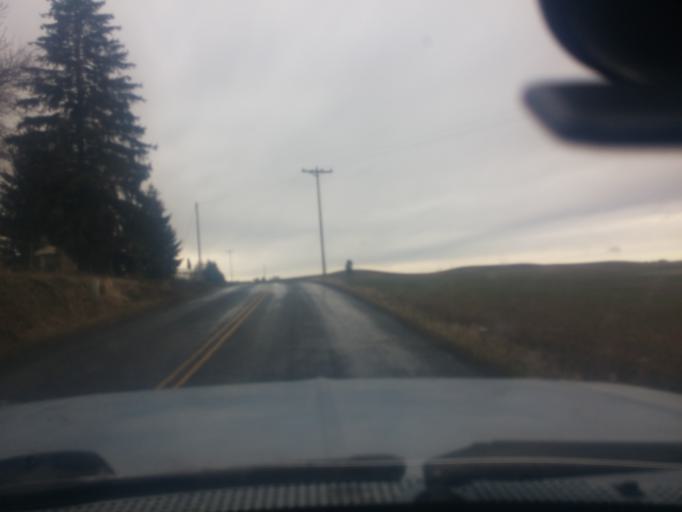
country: US
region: Idaho
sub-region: Latah County
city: Moscow
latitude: 46.9311
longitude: -116.8775
